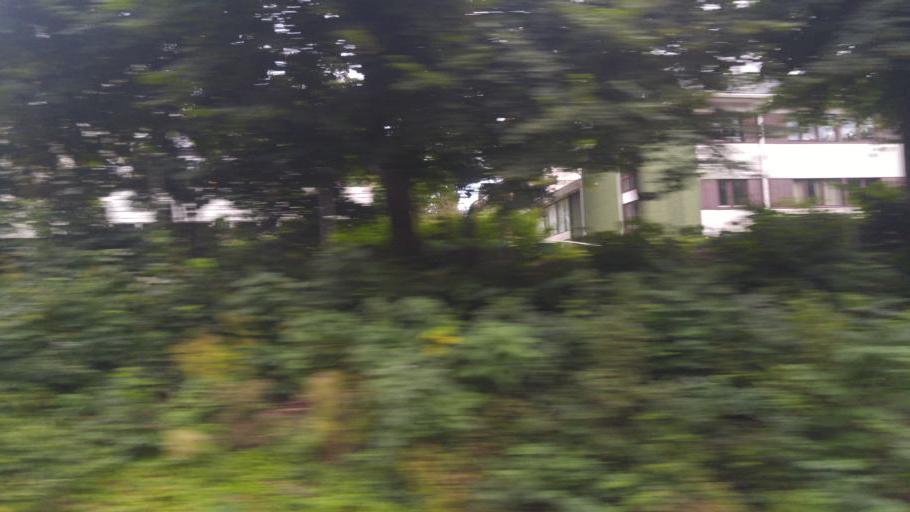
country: NO
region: Oslo
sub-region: Oslo
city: Sjolyststranda
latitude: 59.9519
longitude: 10.6936
